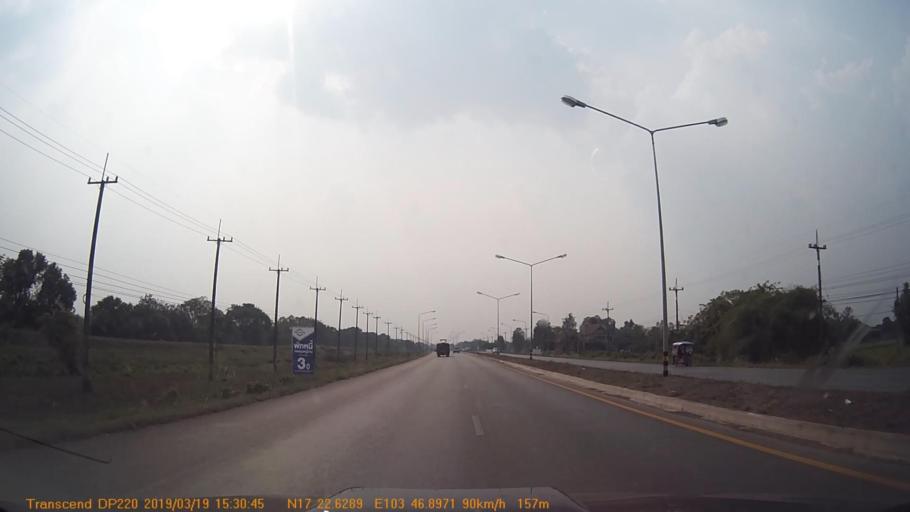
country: TH
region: Sakon Nakhon
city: Phang Khon
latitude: 17.3772
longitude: 103.7813
